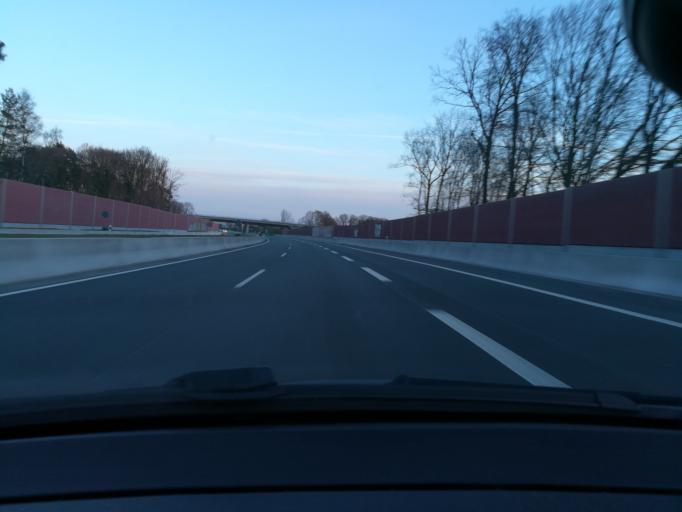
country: DE
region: North Rhine-Westphalia
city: Halle
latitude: 52.0399
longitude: 8.3409
